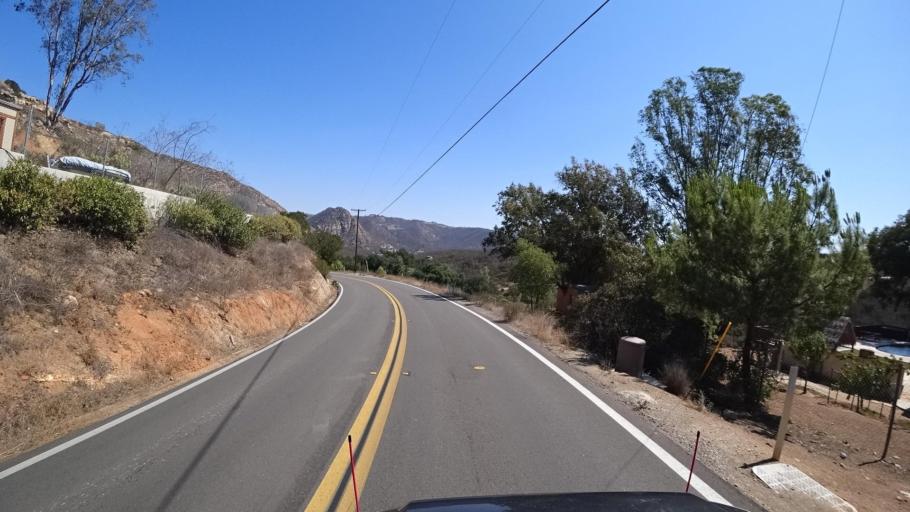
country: US
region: California
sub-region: San Diego County
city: Harbison Canyon
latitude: 32.8272
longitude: -116.8427
